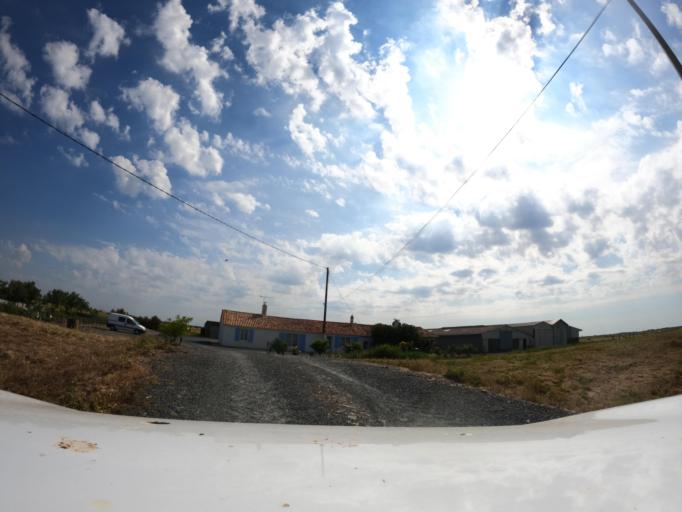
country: FR
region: Poitou-Charentes
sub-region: Departement de la Charente-Maritime
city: Charron
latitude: 46.3237
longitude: -1.1444
